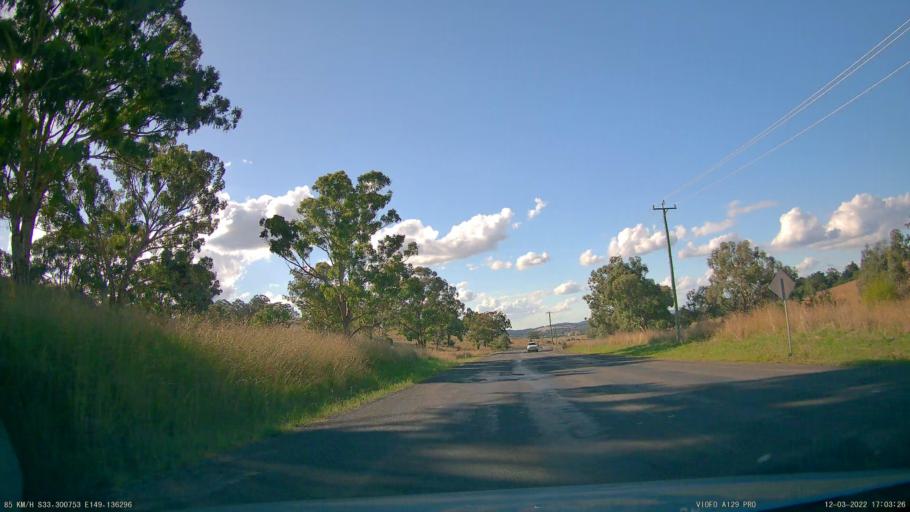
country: AU
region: New South Wales
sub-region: Orange Municipality
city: Orange
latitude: -33.3006
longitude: 149.1362
